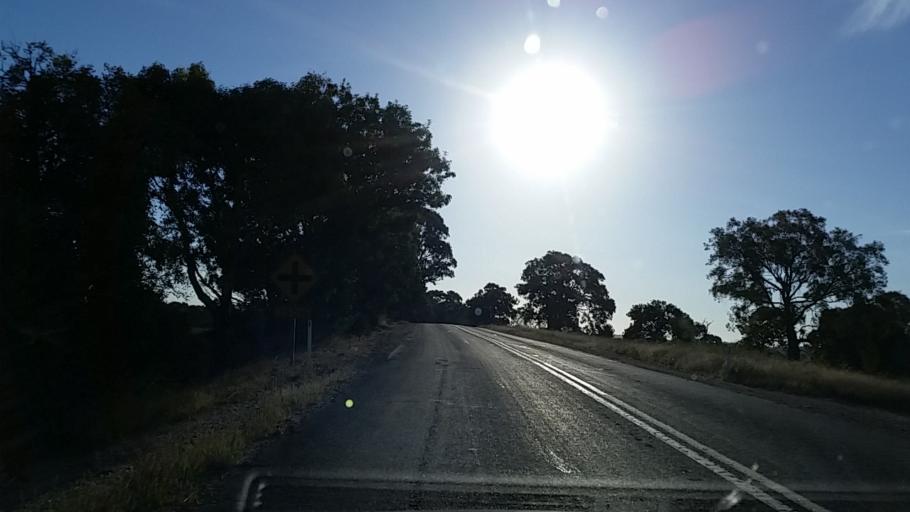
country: AU
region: South Australia
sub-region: Adelaide Hills
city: Birdwood
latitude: -34.7705
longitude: 139.0645
